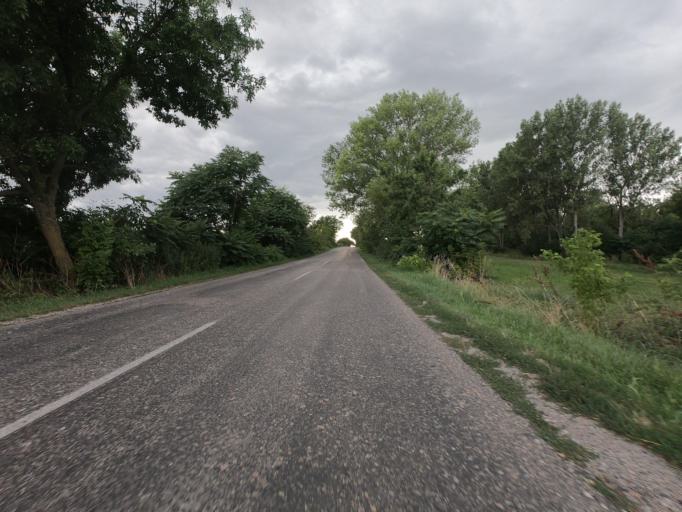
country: HU
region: Heves
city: Poroszlo
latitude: 47.6996
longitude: 20.6503
